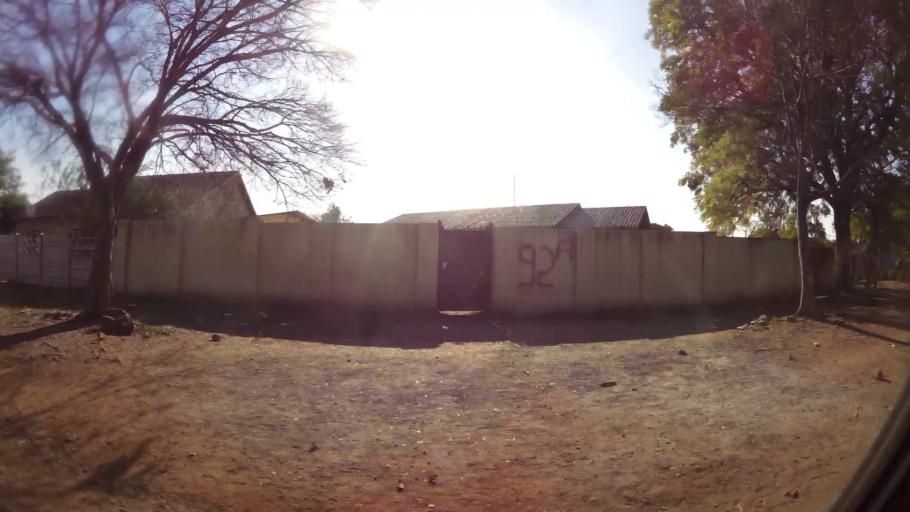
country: ZA
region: North-West
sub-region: Bojanala Platinum District Municipality
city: Rustenburg
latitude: -25.6562
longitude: 27.2288
